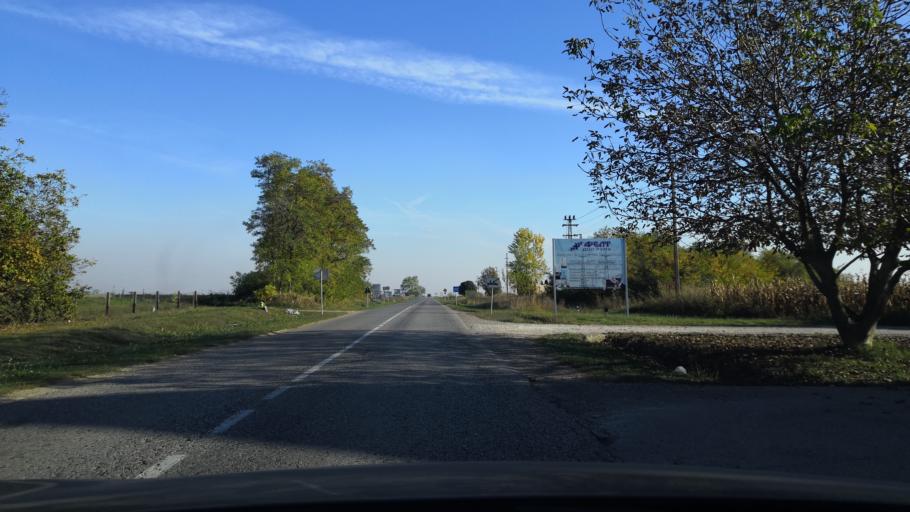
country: RS
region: Autonomna Pokrajina Vojvodina
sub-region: Sremski Okrug
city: Ruma
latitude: 45.0007
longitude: 19.8455
